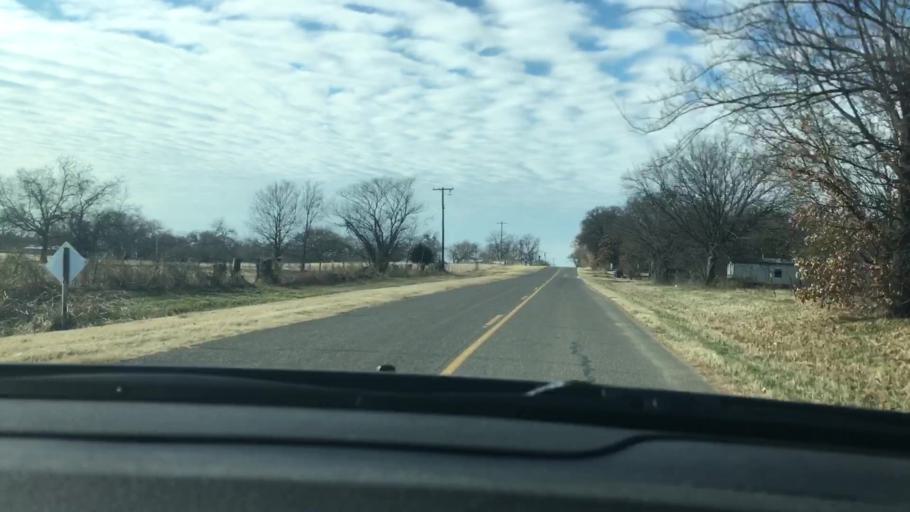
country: US
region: Oklahoma
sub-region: Garvin County
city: Pauls Valley
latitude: 34.7386
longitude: -97.1481
